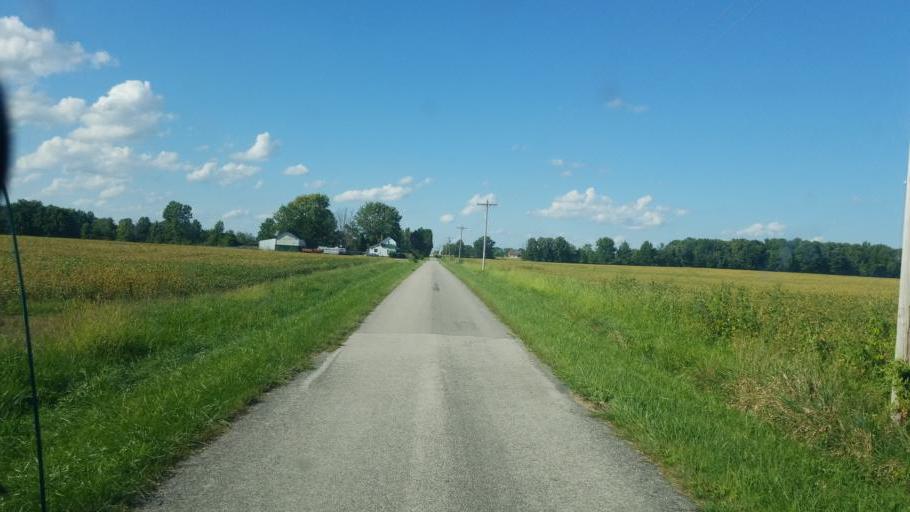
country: US
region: Ohio
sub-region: Marion County
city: Marion
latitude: 40.6244
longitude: -83.2694
